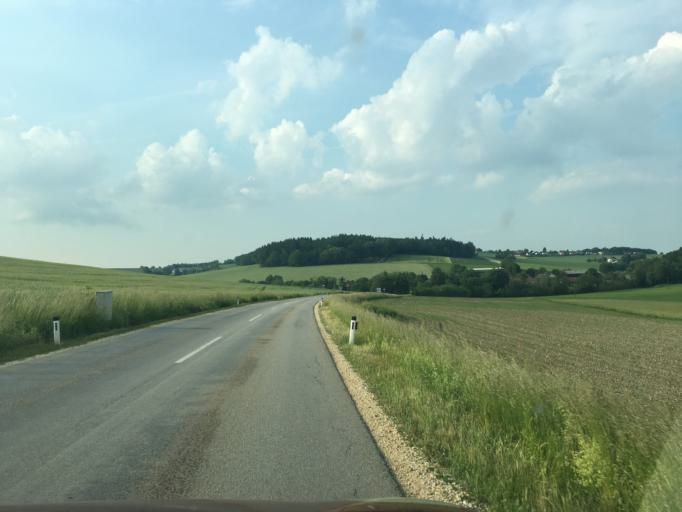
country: AT
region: Upper Austria
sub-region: Politischer Bezirk Ried im Innkreis
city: Ried im Innkreis
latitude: 48.1866
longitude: 13.5753
